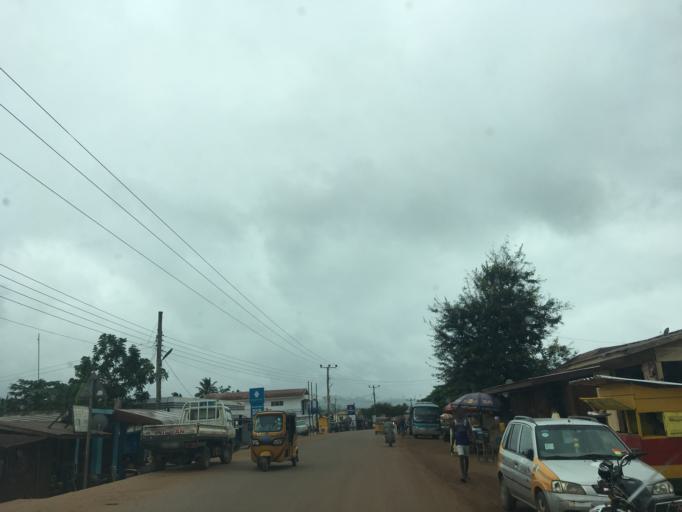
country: GH
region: Western
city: Wassa-Akropong
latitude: 5.8066
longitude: -2.4335
